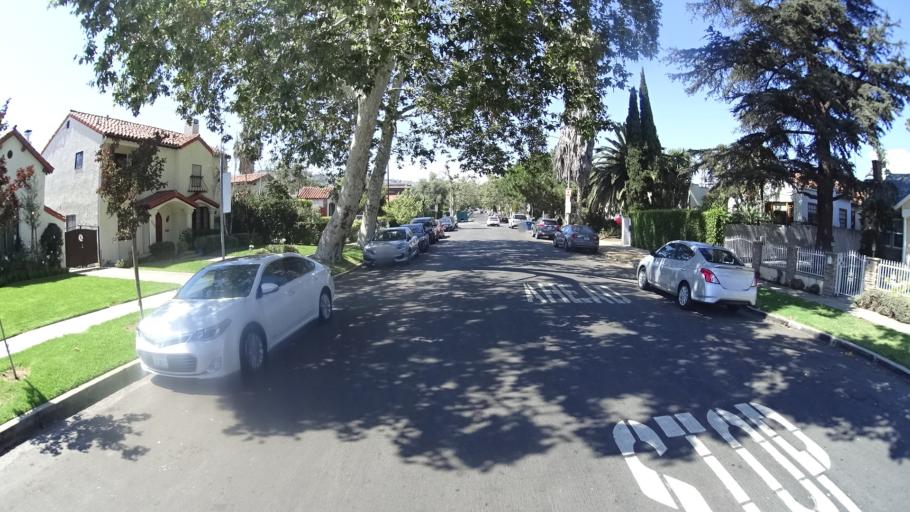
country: US
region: California
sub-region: Los Angeles County
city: West Hollywood
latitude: 34.0810
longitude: -118.3638
